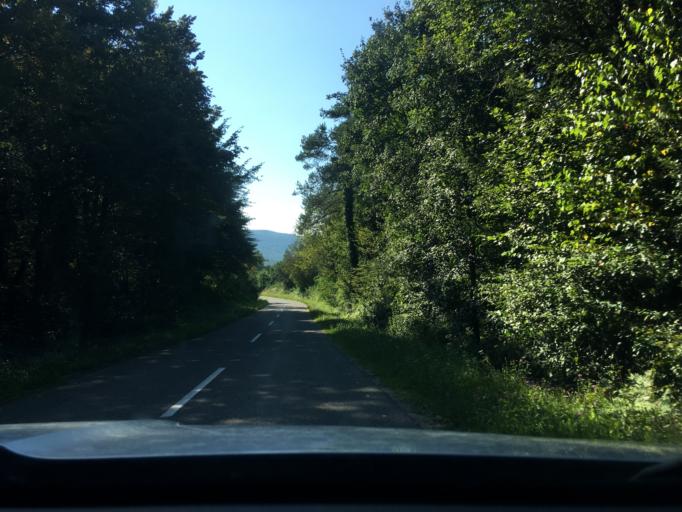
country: SI
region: Crnomelj
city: Crnomelj
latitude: 45.4574
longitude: 15.2275
